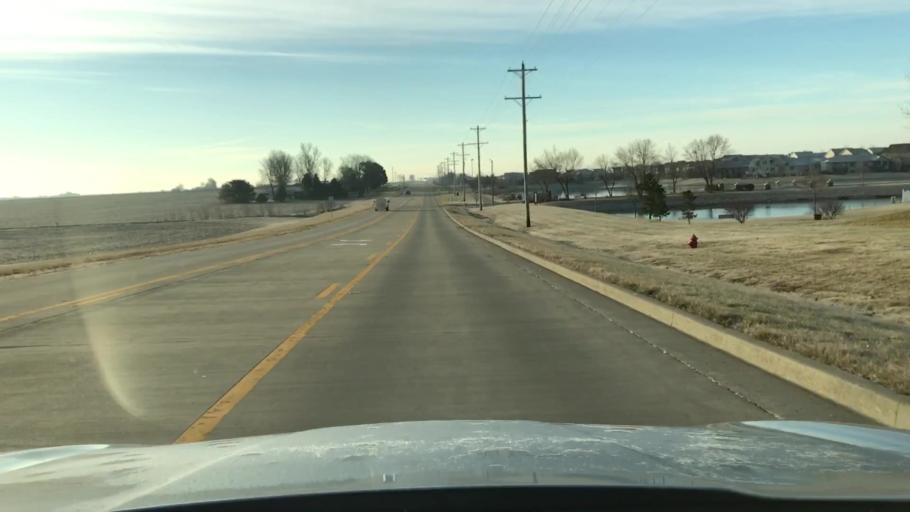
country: US
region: Illinois
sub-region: McLean County
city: Hudson
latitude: 40.5586
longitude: -88.9446
